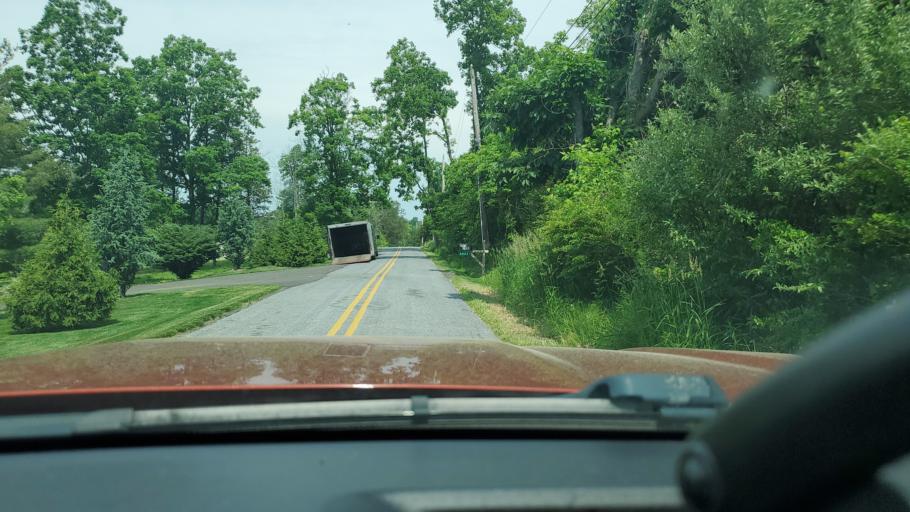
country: US
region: Pennsylvania
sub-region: Montgomery County
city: Woxall
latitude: 40.3120
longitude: -75.5011
